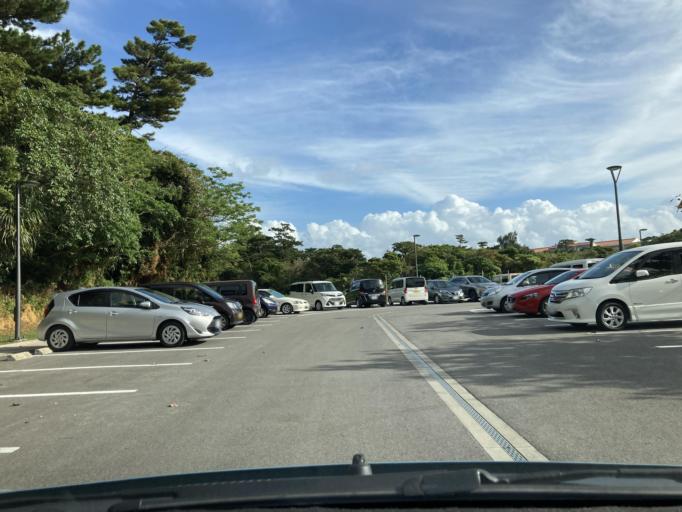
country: JP
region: Okinawa
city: Katsuren-haebaru
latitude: 26.3332
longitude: 127.8808
